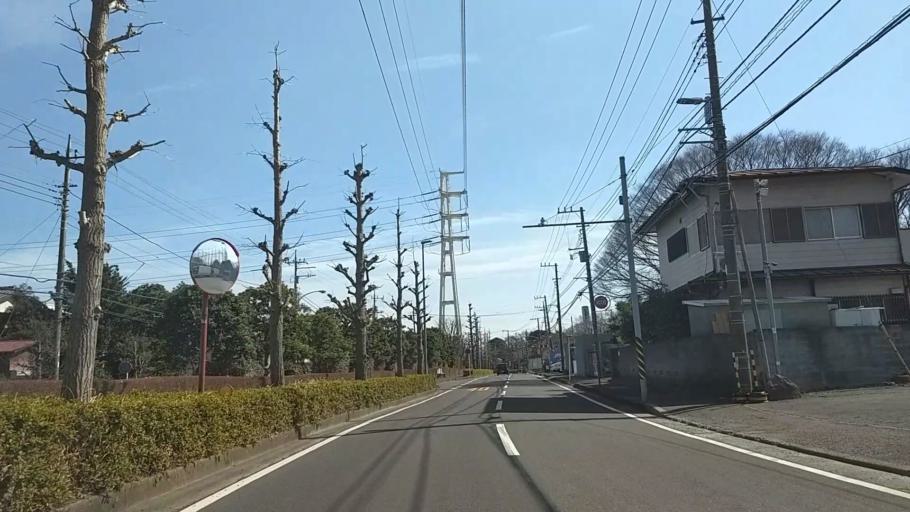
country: JP
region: Kanagawa
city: Fujisawa
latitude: 35.3694
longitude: 139.4311
